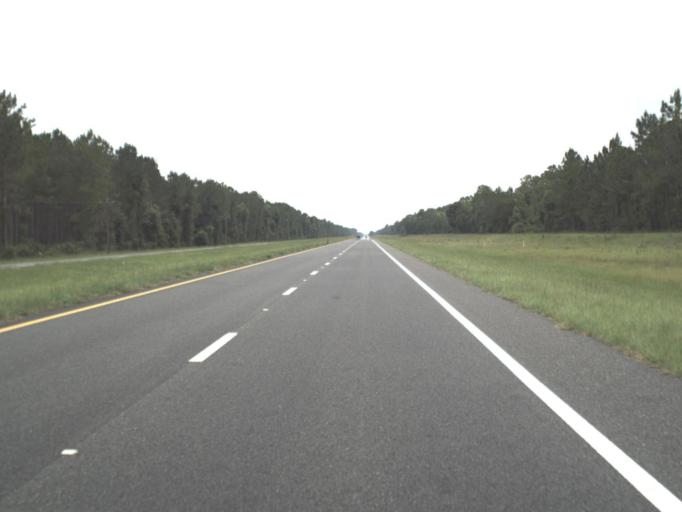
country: US
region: Florida
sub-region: Levy County
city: Chiefland
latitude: 29.3779
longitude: -82.7993
